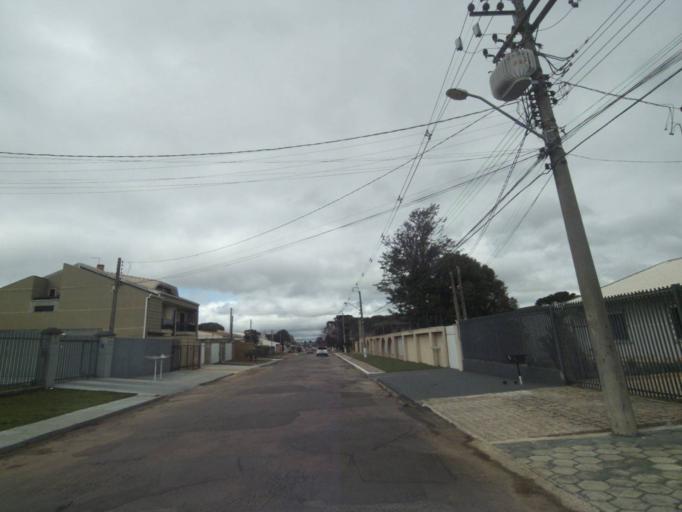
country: BR
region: Parana
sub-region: Sao Jose Dos Pinhais
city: Sao Jose dos Pinhais
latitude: -25.5369
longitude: -49.2969
